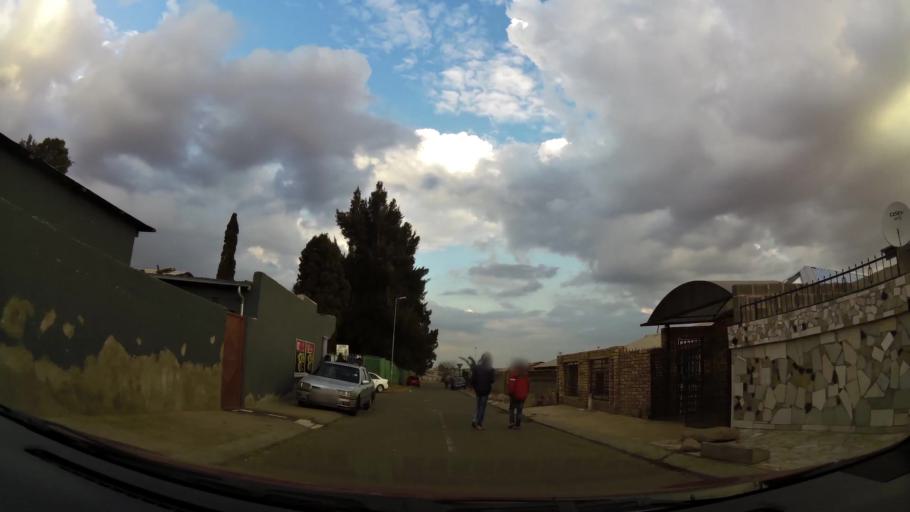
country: ZA
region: Gauteng
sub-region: City of Johannesburg Metropolitan Municipality
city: Soweto
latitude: -26.2454
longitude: 27.8248
